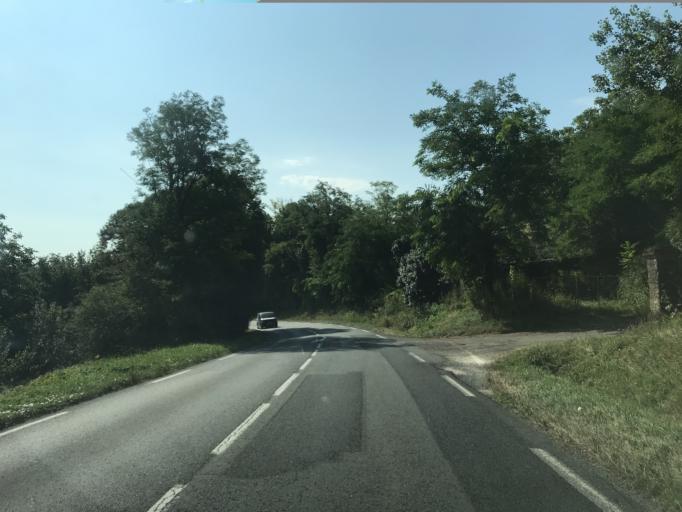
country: FR
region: Aquitaine
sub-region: Departement de la Dordogne
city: Sarlat-la-Caneda
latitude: 44.9041
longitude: 1.2023
